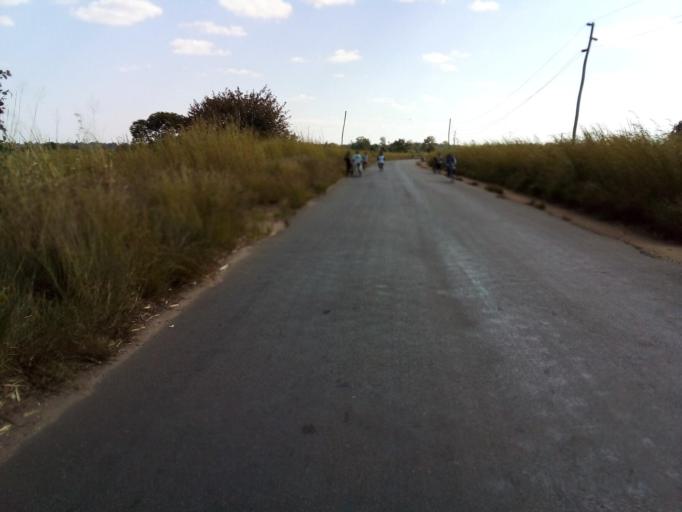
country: MZ
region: Zambezia
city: Quelimane
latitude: -17.5779
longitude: 36.6834
